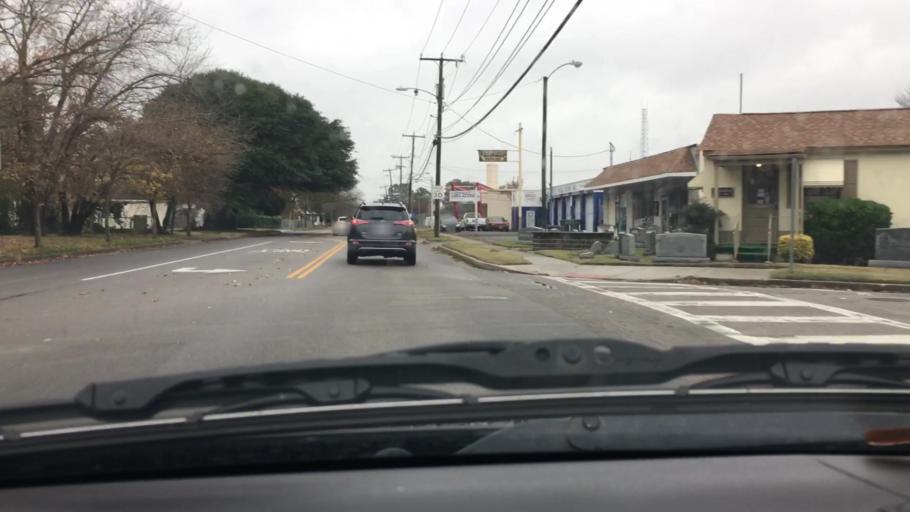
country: US
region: Virginia
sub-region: City of Norfolk
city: Norfolk
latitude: 36.8784
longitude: -76.2529
